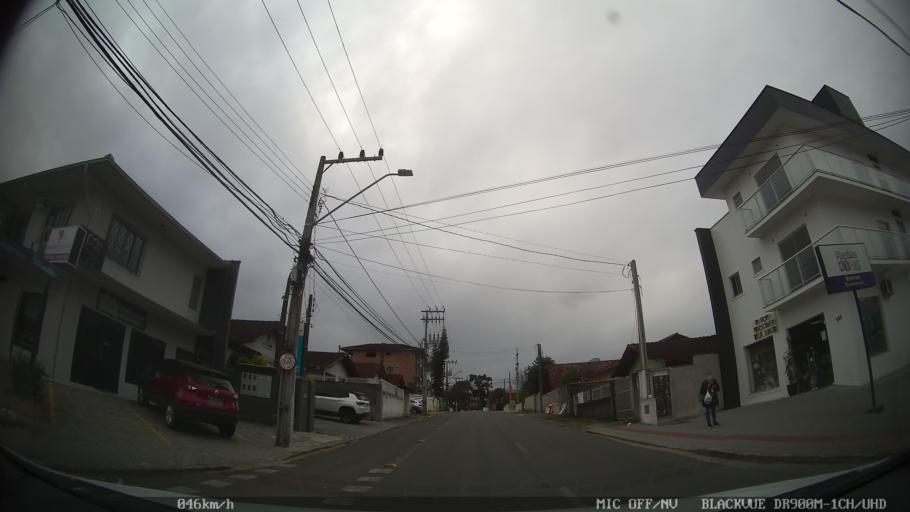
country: BR
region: Santa Catarina
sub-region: Joinville
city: Joinville
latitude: -26.2749
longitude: -48.8743
